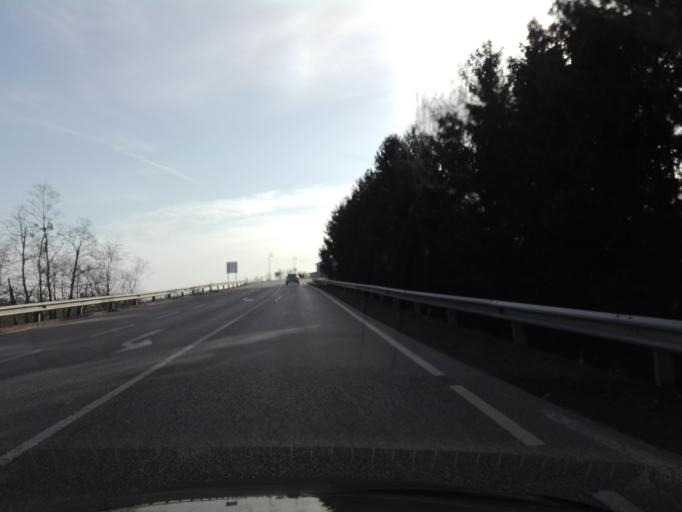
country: AT
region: Lower Austria
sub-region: Politischer Bezirk Amstetten
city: Strengberg
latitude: 48.1464
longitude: 14.6359
